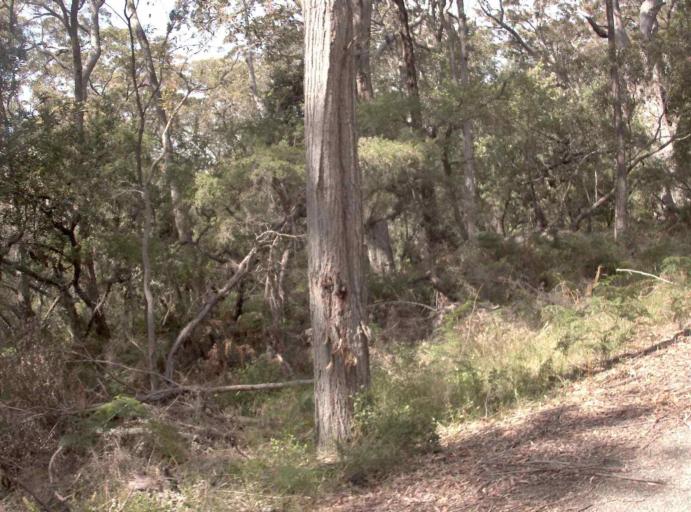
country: AU
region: New South Wales
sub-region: Bega Valley
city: Eden
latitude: -37.5433
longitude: 149.7099
